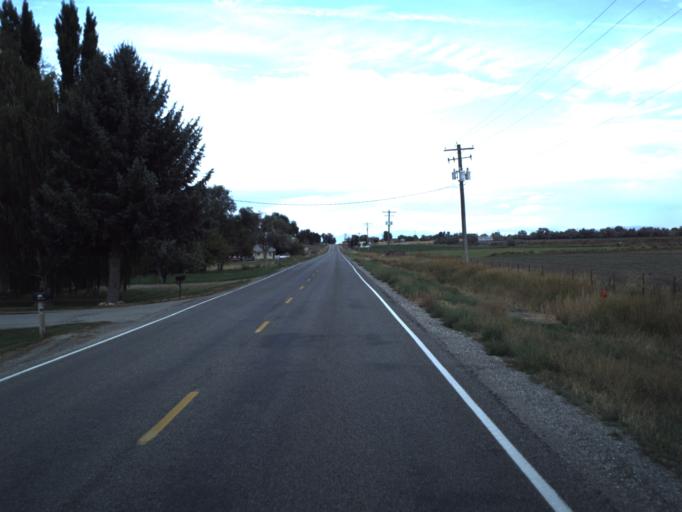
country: US
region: Utah
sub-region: Cache County
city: Lewiston
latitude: 41.9784
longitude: -111.9542
